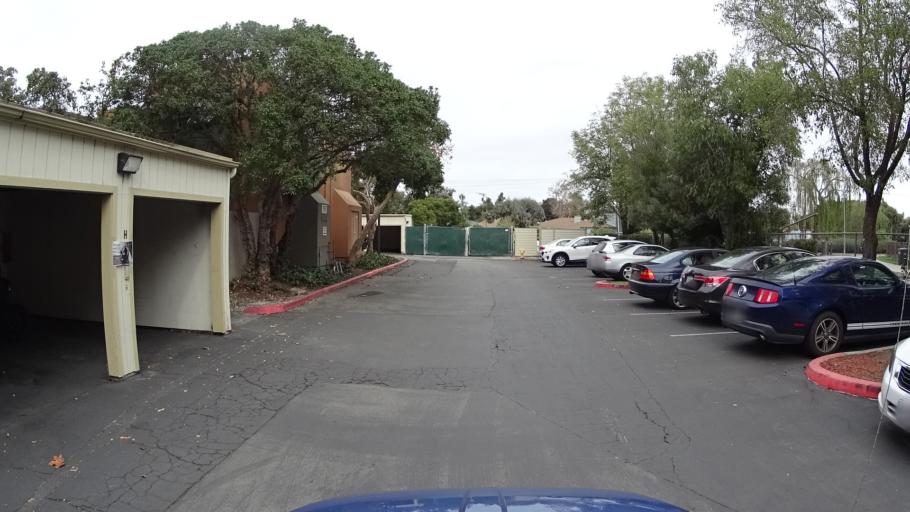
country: US
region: California
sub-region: San Mateo County
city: Belmont
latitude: 37.5332
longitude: -122.2824
